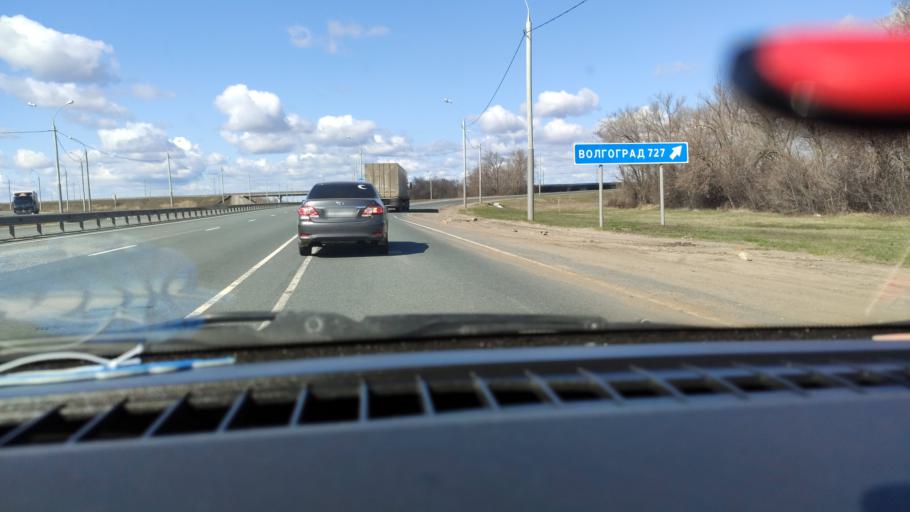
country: RU
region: Samara
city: Varlamovo
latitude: 53.1975
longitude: 48.2943
